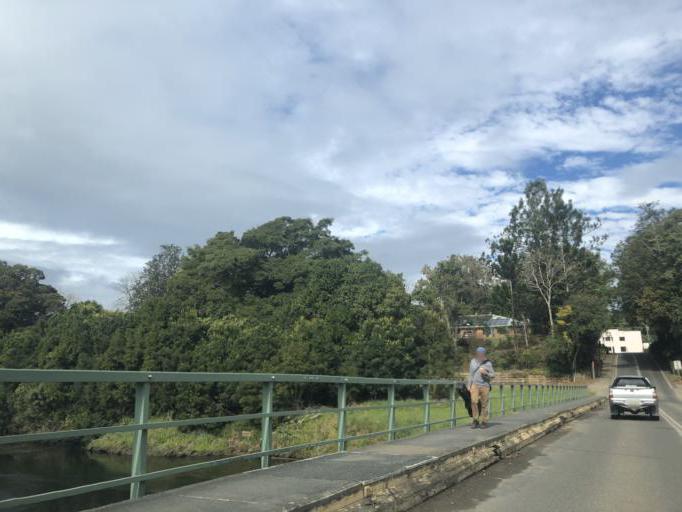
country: AU
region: New South Wales
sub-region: Bellingen
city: Bellingen
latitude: -30.4505
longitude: 152.8985
